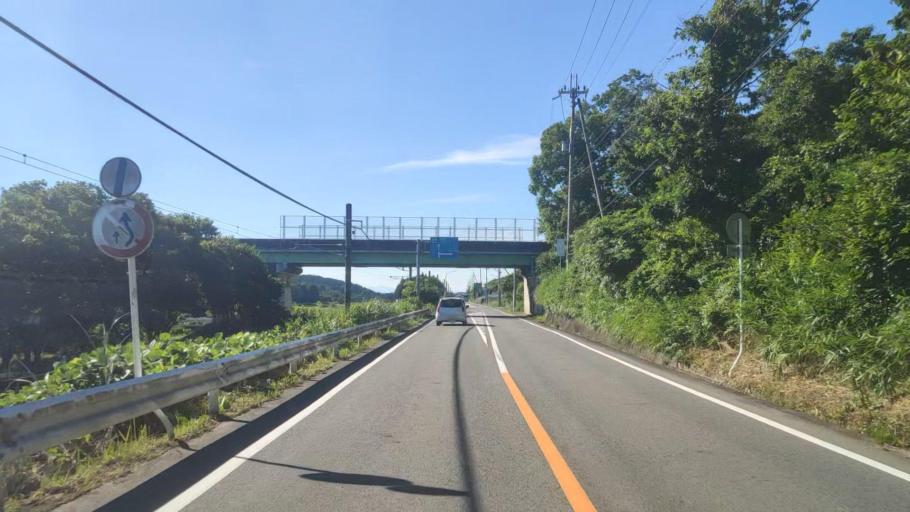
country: JP
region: Shiga Prefecture
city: Minakuchicho-matoba
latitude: 34.8757
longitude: 136.2397
